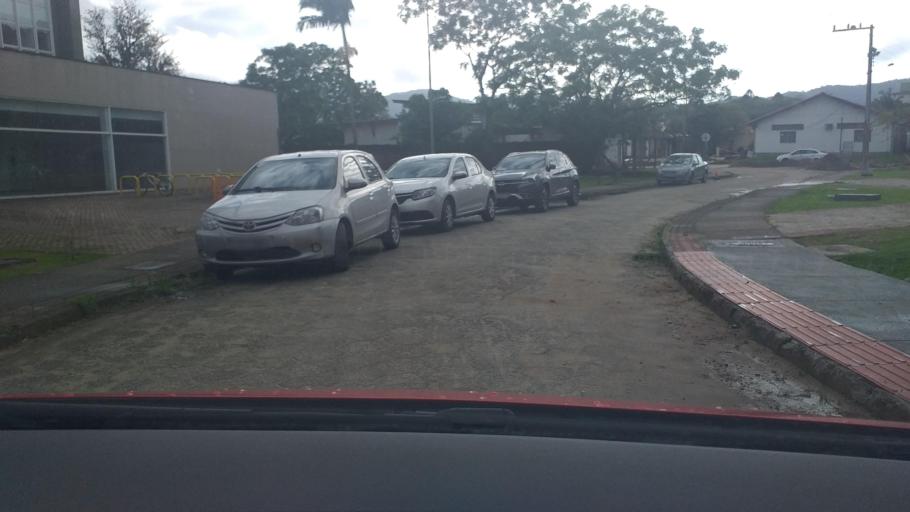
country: BR
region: Santa Catarina
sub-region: Florianopolis
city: Corrego Grande
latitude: -27.5987
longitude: -48.5148
